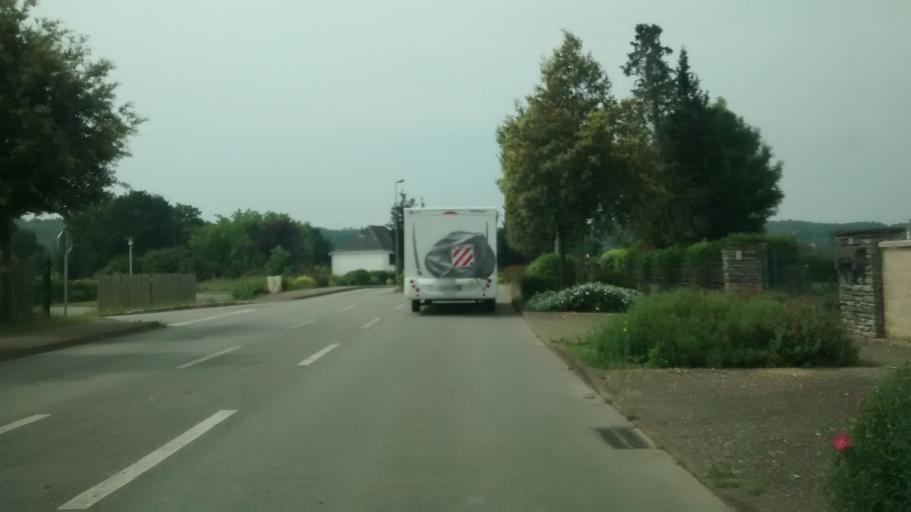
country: FR
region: Brittany
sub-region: Departement du Morbihan
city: Malestroit
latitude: 47.8125
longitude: -2.3731
